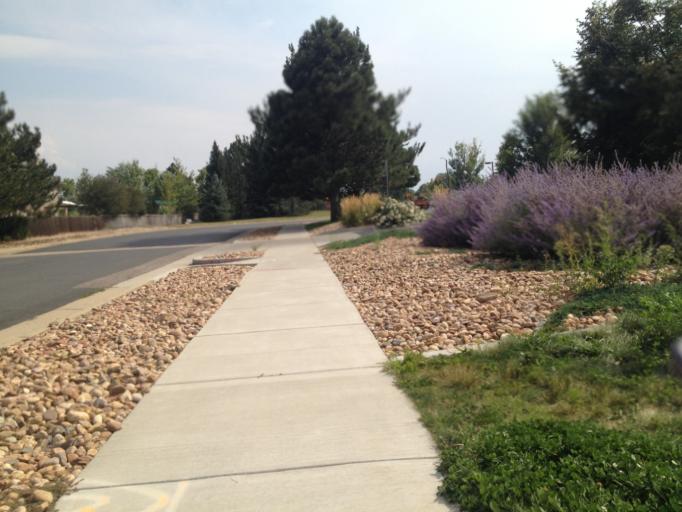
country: US
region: Colorado
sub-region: Boulder County
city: Louisville
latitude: 39.9882
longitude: -105.1542
